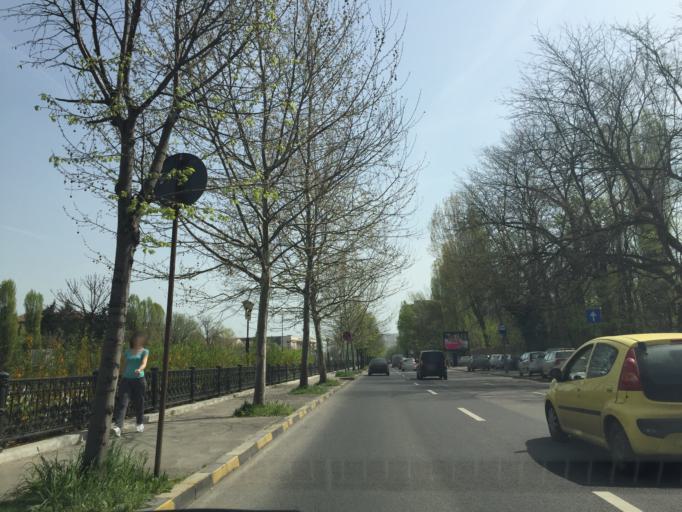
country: RO
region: Bucuresti
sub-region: Municipiul Bucuresti
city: Bucuresti
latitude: 44.4408
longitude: 26.0654
